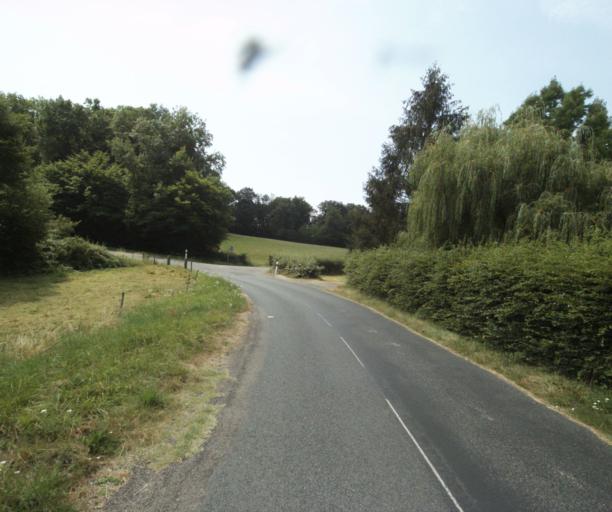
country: FR
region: Bourgogne
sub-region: Departement de Saone-et-Loire
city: Gueugnon
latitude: 46.5900
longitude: 4.0808
